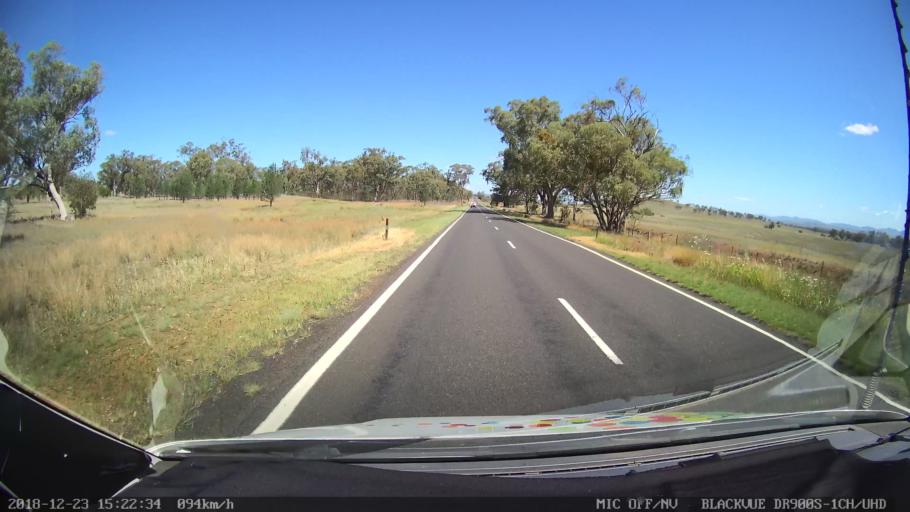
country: AU
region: New South Wales
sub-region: Tamworth Municipality
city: Manilla
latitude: -30.8698
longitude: 150.8060
